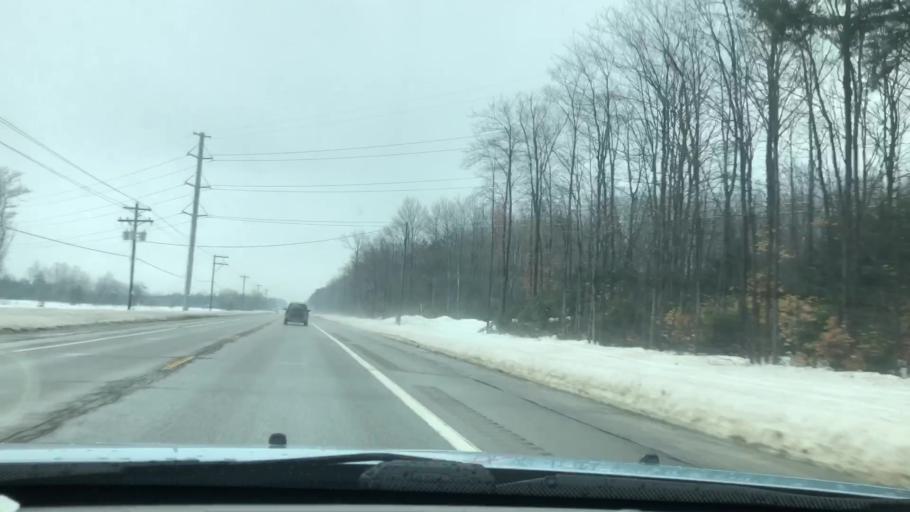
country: US
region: Michigan
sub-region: Otsego County
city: Gaylord
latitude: 45.0277
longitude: -84.7552
